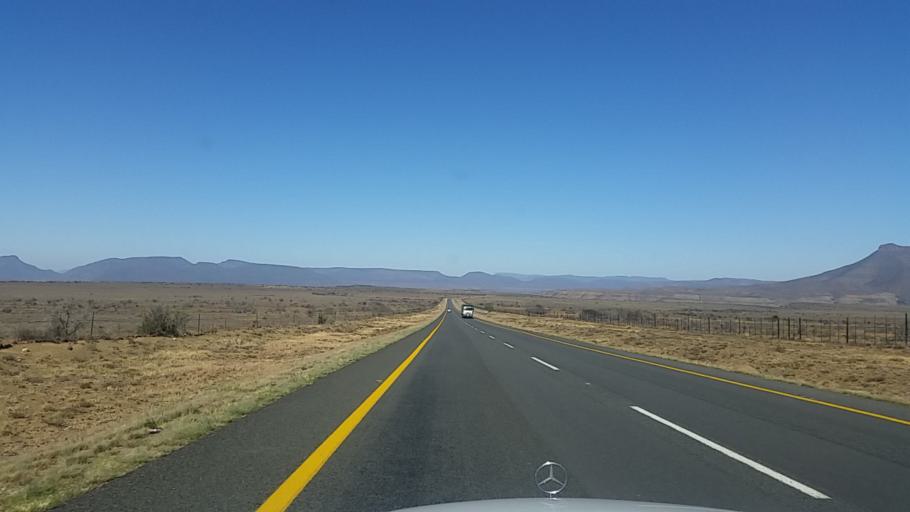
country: ZA
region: Eastern Cape
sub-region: Cacadu District Municipality
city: Graaff-Reinet
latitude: -32.1209
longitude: 24.6038
